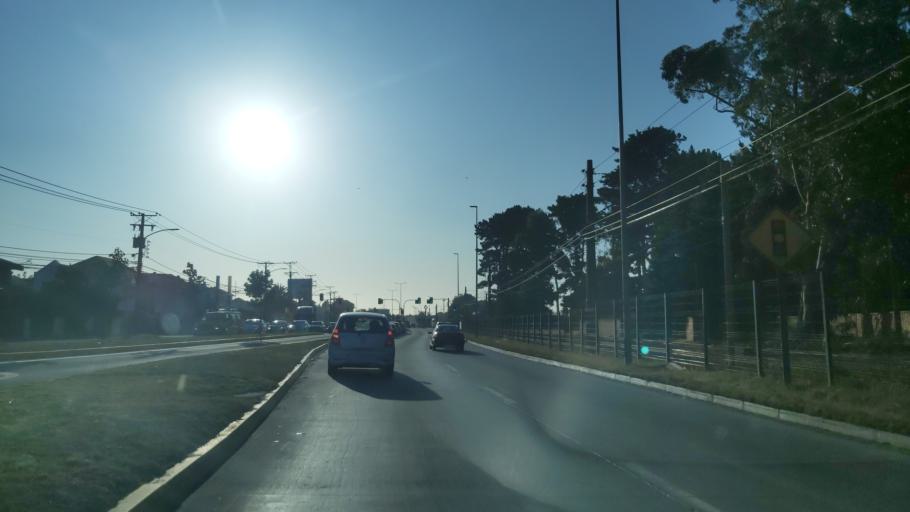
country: CL
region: Biobio
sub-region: Provincia de Concepcion
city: Concepcion
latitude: -36.8387
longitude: -73.0940
